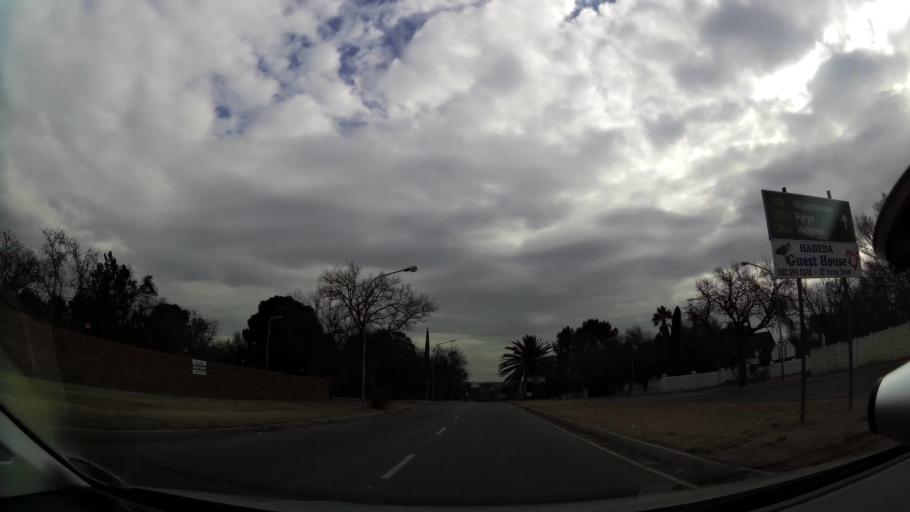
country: ZA
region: Orange Free State
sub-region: Fezile Dabi District Municipality
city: Kroonstad
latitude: -27.6753
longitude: 27.2393
